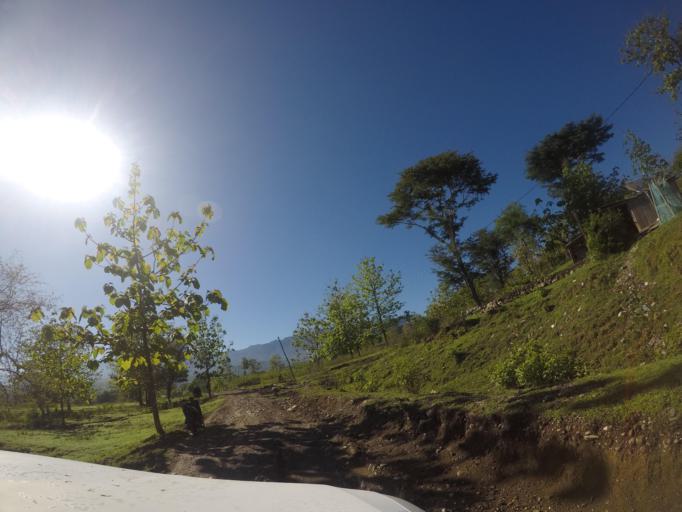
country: TL
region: Bobonaro
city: Maliana
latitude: -8.9965
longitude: 125.1886
